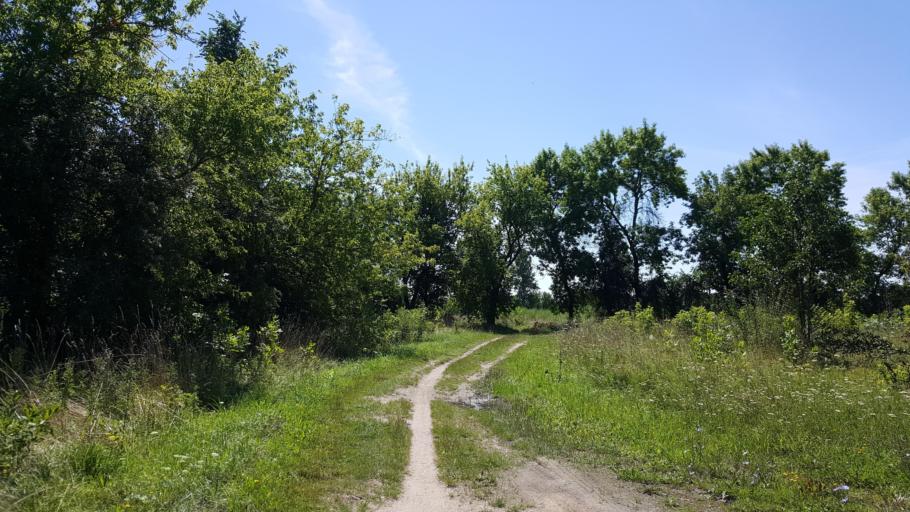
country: BY
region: Brest
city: Charnawchytsy
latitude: 52.2186
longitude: 23.7448
